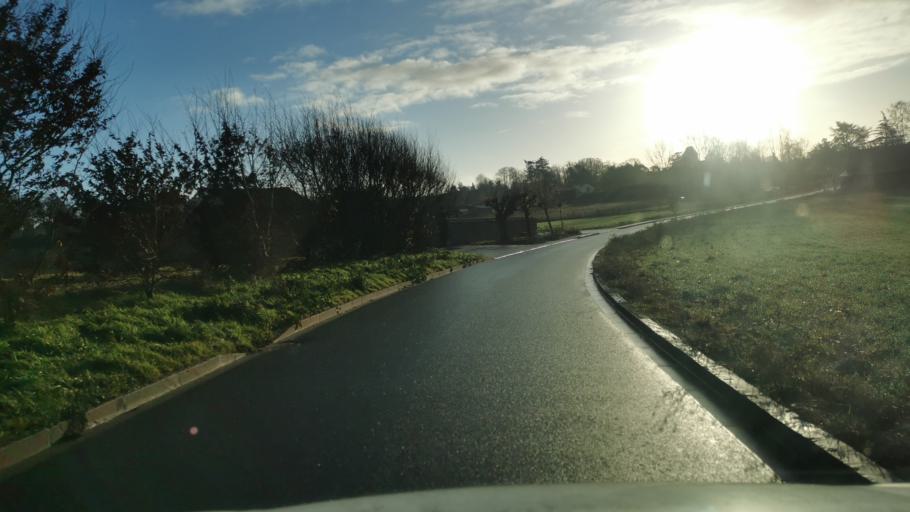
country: FR
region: Ile-de-France
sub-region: Departement des Yvelines
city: Bazainville
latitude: 48.8069
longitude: 1.6644
